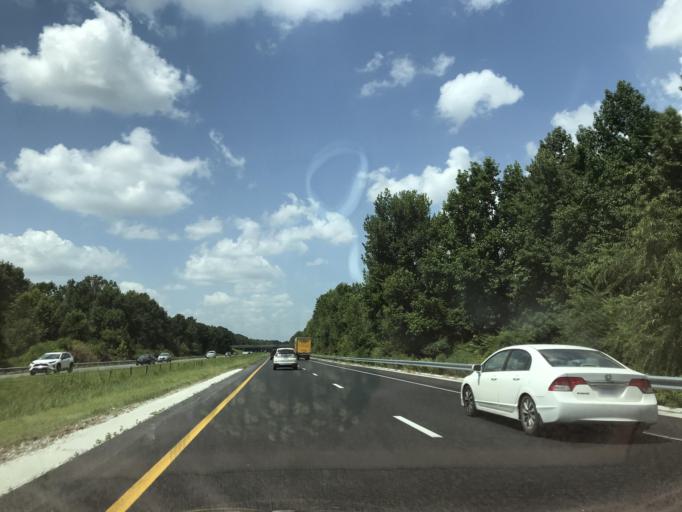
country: US
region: North Carolina
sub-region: Duplin County
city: Warsaw
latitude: 34.9683
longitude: -78.1140
